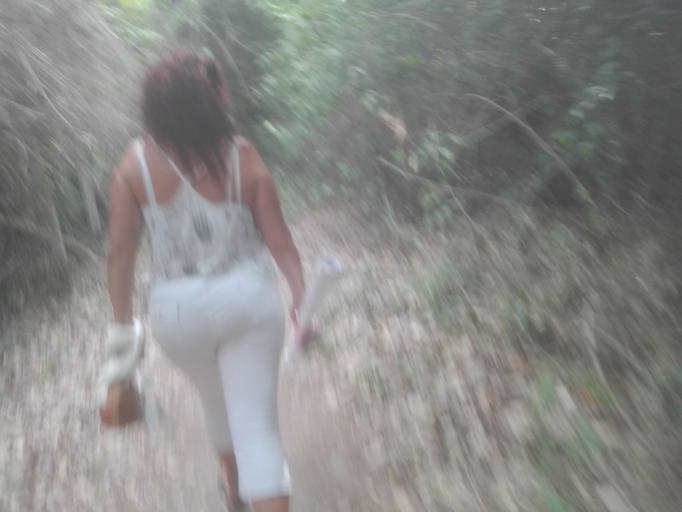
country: CO
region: Bolivar
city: Turbana
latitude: 10.1733
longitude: -75.7457
